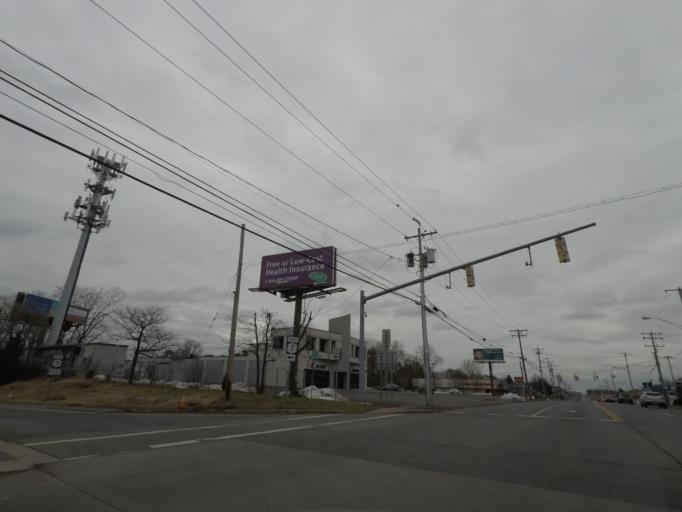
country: US
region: New York
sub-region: Schenectady County
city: Schenectady
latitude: 42.7854
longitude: -73.9097
